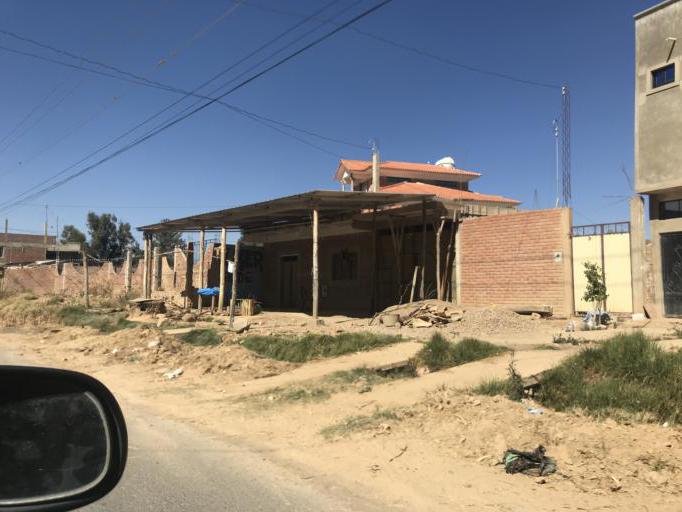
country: BO
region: Cochabamba
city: Cliza
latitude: -17.5952
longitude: -65.9478
